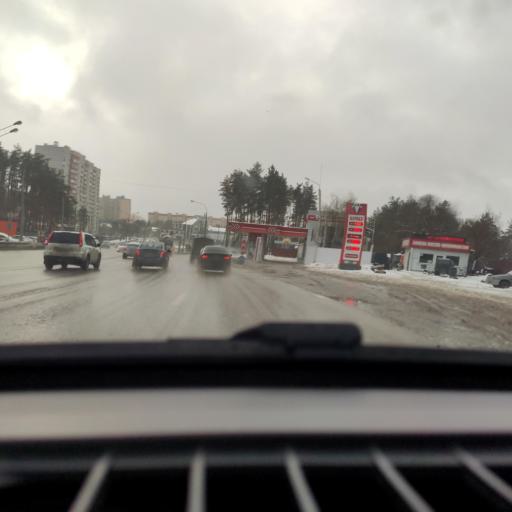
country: RU
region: Voronezj
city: Pridonskoy
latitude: 51.6864
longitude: 39.1179
